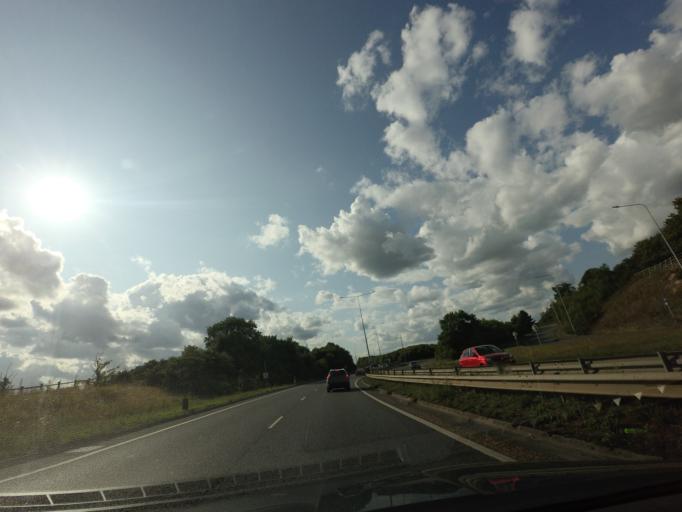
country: GB
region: England
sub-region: Kent
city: Harrietsham
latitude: 51.2600
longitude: 0.6141
